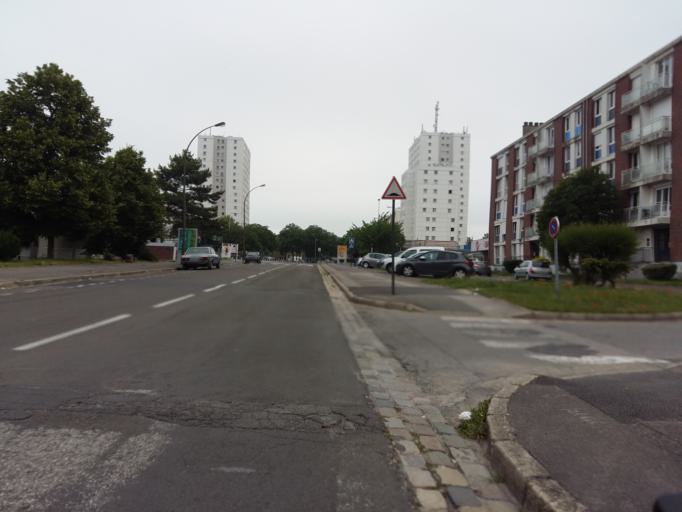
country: FR
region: Picardie
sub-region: Departement de la Somme
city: Amiens
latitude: 49.9093
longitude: 2.3005
